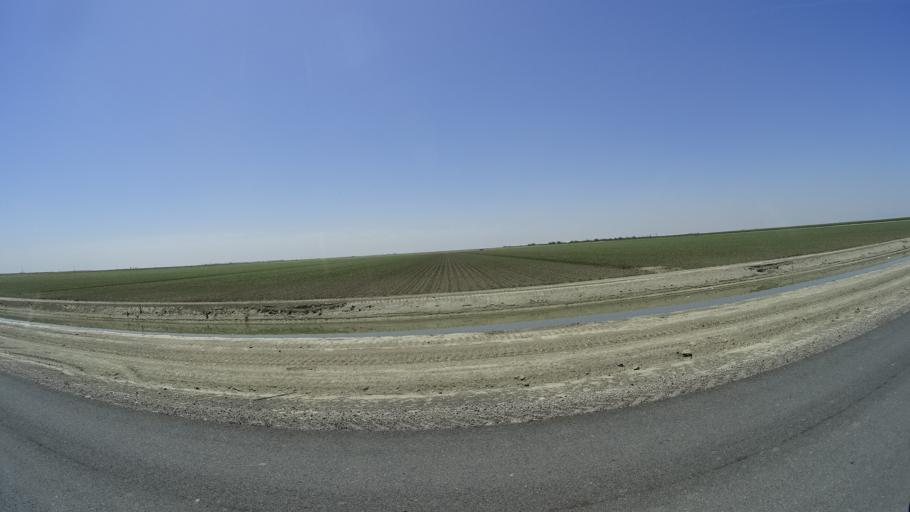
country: US
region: California
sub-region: Kings County
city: Corcoran
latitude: 36.0217
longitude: -119.5416
